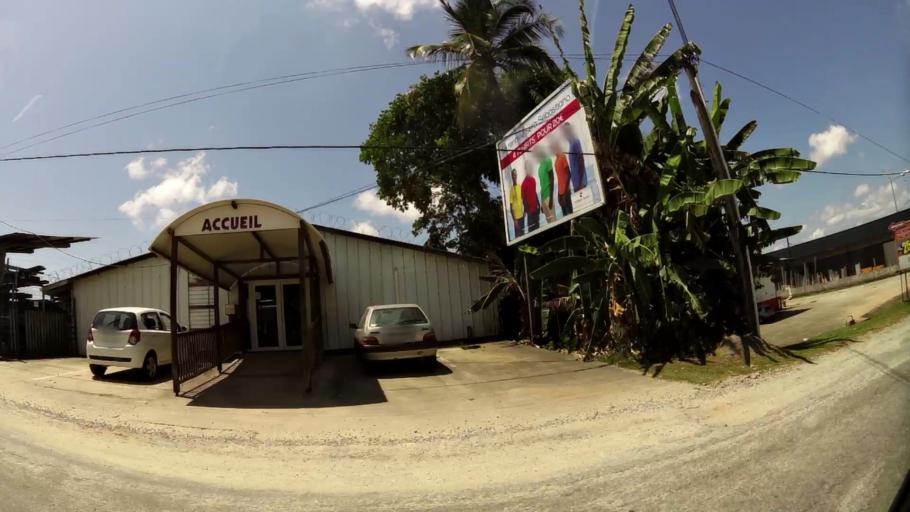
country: GF
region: Guyane
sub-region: Guyane
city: Cayenne
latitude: 4.9069
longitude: -52.3246
